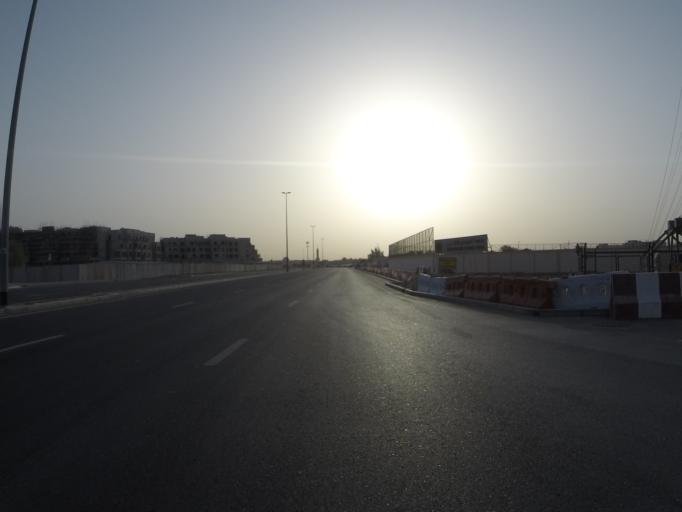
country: AE
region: Dubai
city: Dubai
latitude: 25.1512
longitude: 55.2519
